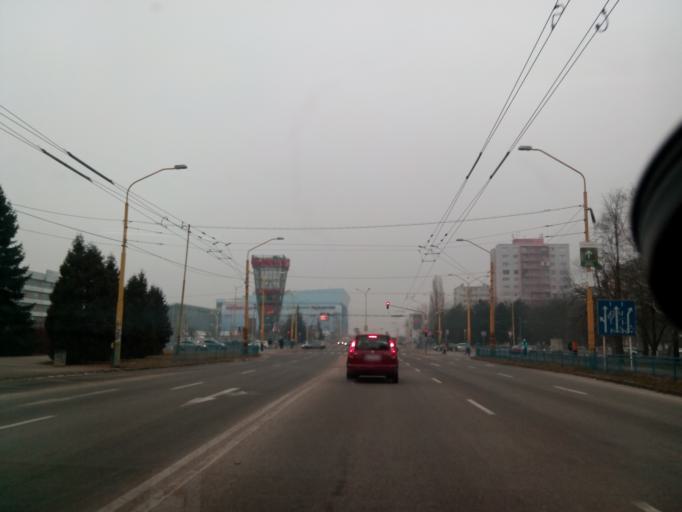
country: SK
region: Kosicky
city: Kosice
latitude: 48.7133
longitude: 21.2341
